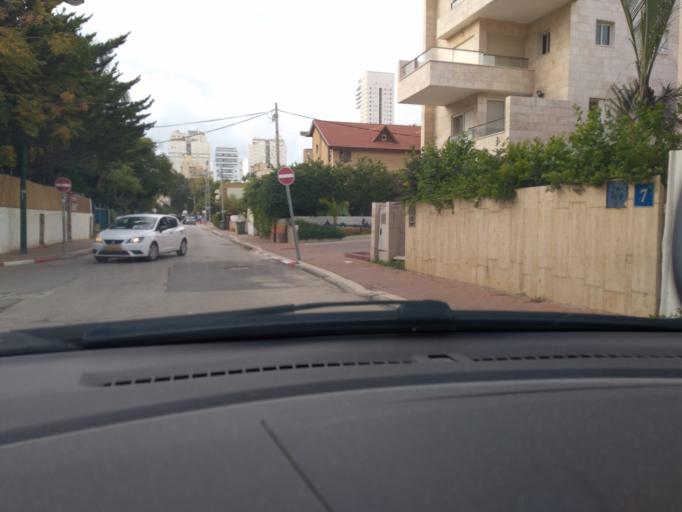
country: IL
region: Central District
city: Netanya
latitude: 32.3375
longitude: 34.8577
